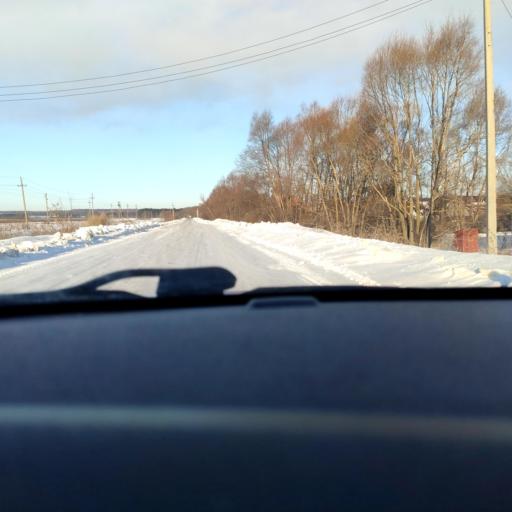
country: RU
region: Bashkortostan
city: Mikhaylovka
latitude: 54.7735
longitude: 55.8259
